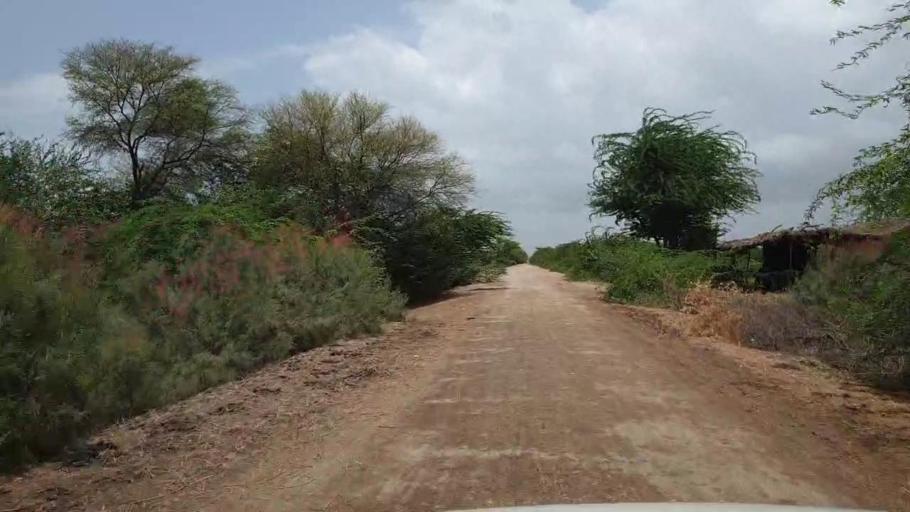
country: PK
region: Sindh
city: Kario
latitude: 24.6960
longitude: 68.6435
